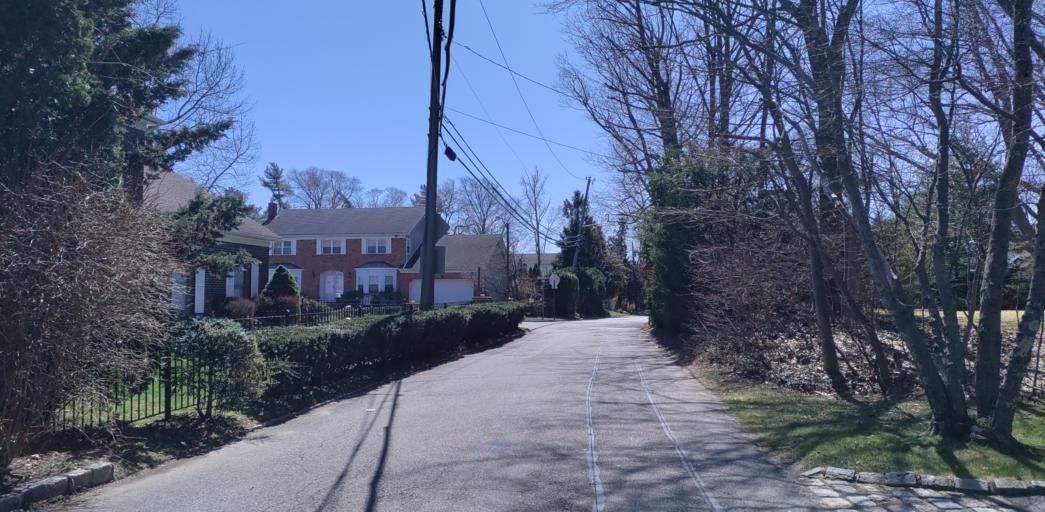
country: US
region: New York
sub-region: Nassau County
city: Greenvale
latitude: 40.8128
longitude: -73.6223
